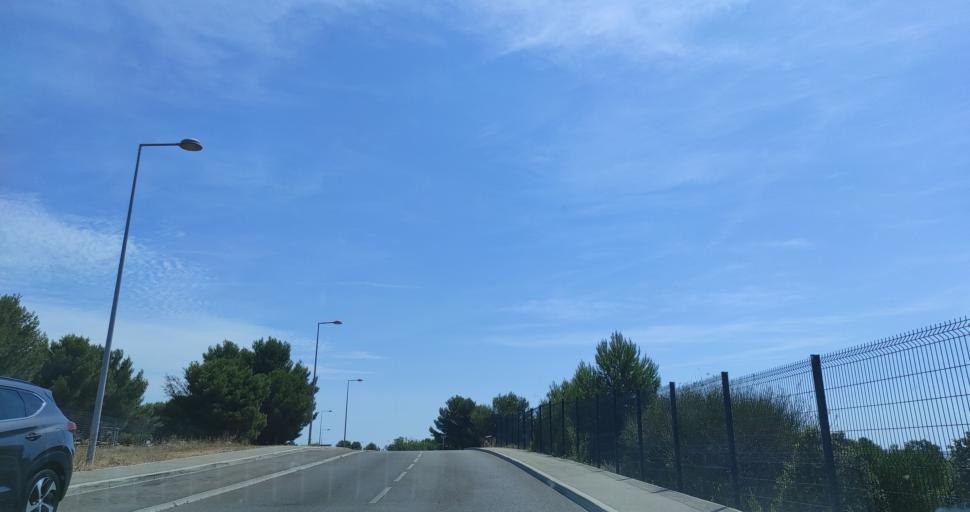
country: FR
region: Provence-Alpes-Cote d'Azur
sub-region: Departement des Bouches-du-Rhone
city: Martigues
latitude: 43.4177
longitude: 5.0385
